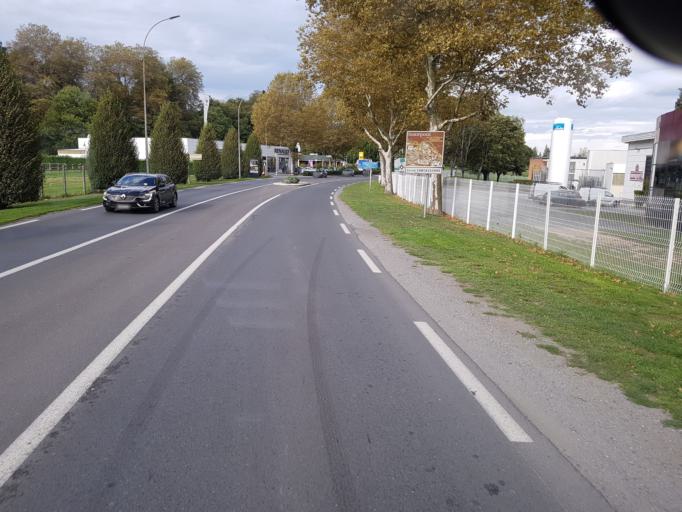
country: FR
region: Midi-Pyrenees
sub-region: Departement du Tarn
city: Mazamet
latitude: 43.4982
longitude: 2.3888
